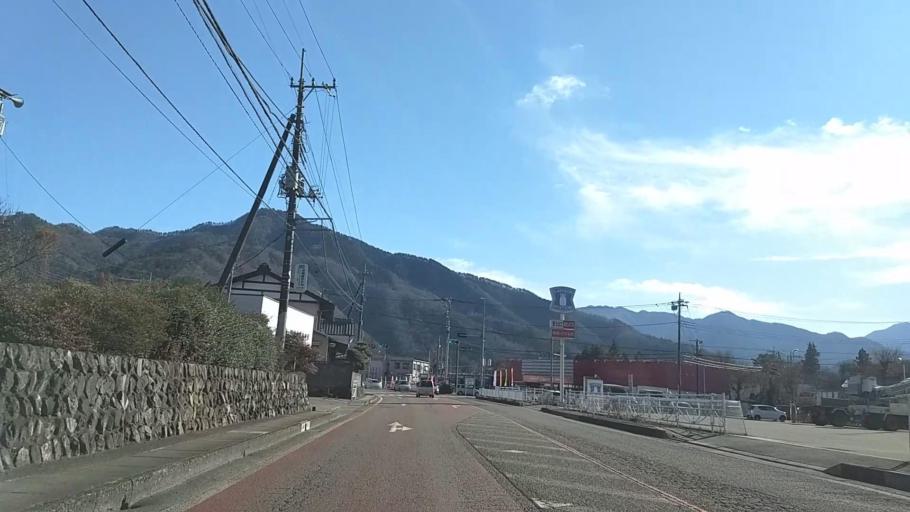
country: JP
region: Yamanashi
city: Otsuki
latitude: 35.5914
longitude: 138.9304
